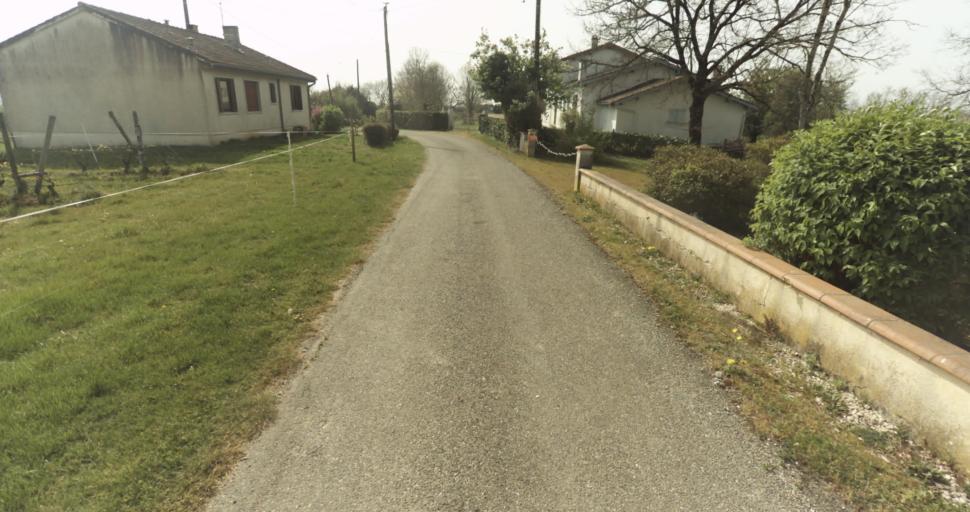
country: FR
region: Midi-Pyrenees
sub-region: Departement du Tarn-et-Garonne
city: Moissac
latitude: 44.1207
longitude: 1.0793
